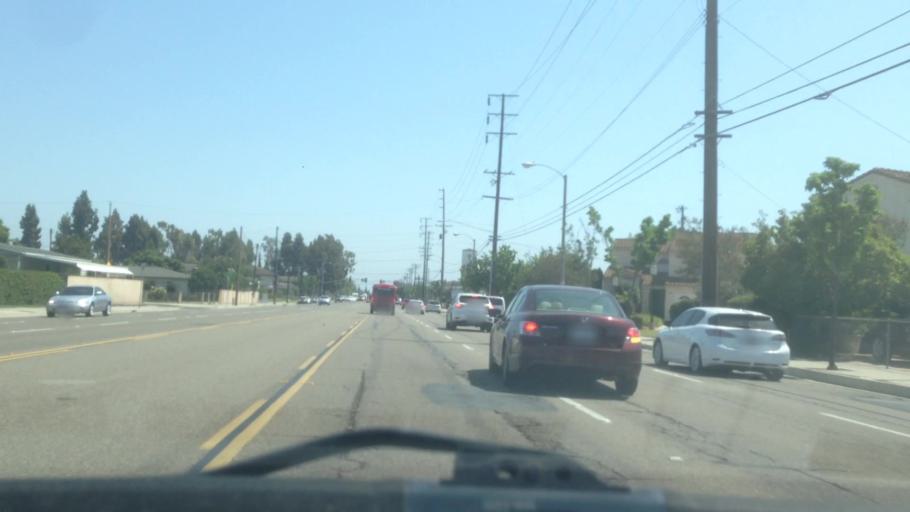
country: US
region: California
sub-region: Orange County
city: Garden Grove
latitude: 33.7408
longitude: -117.9375
